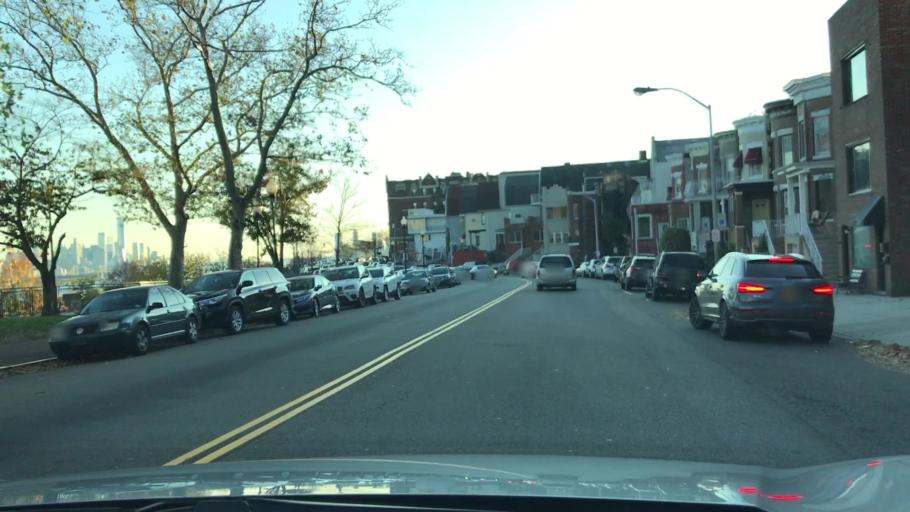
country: US
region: New Jersey
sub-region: Hudson County
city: West New York
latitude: 40.7815
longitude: -74.0113
